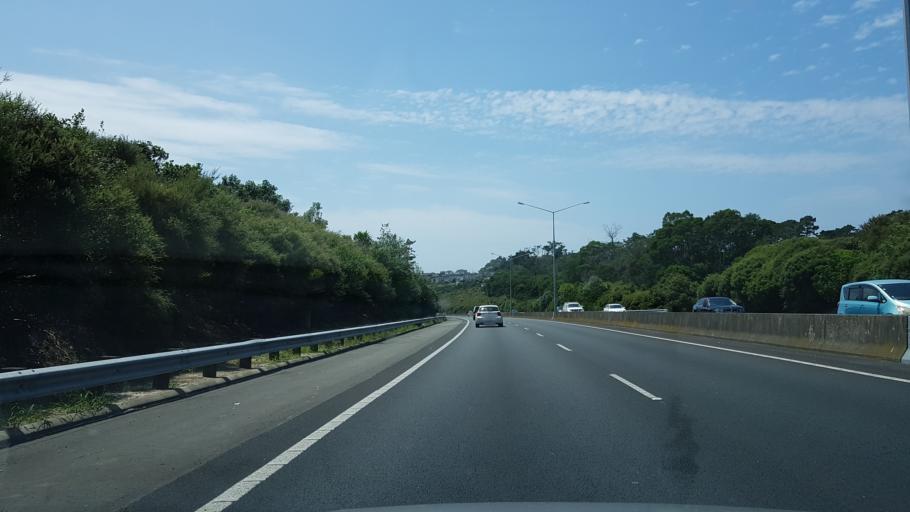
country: NZ
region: Auckland
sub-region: Auckland
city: North Shore
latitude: -36.7780
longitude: 174.6815
